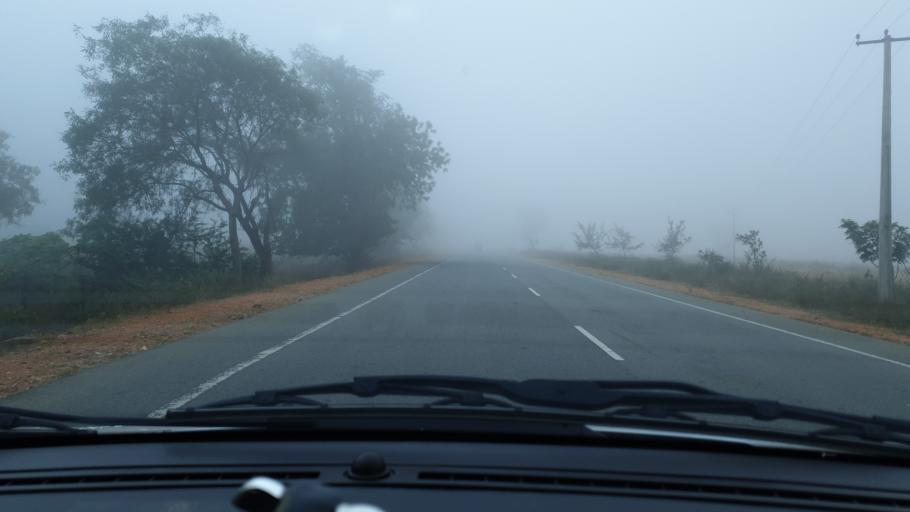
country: IN
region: Telangana
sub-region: Mahbubnagar
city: Nagar Karnul
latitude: 16.6963
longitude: 78.5172
